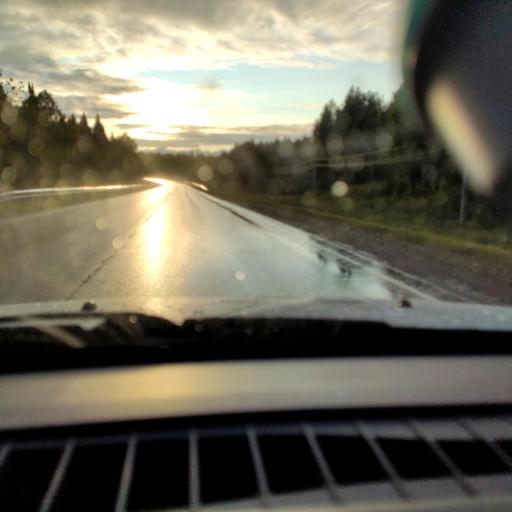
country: RU
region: Perm
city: Verkhnechusovskiye Gorodki
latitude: 58.2546
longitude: 57.0034
